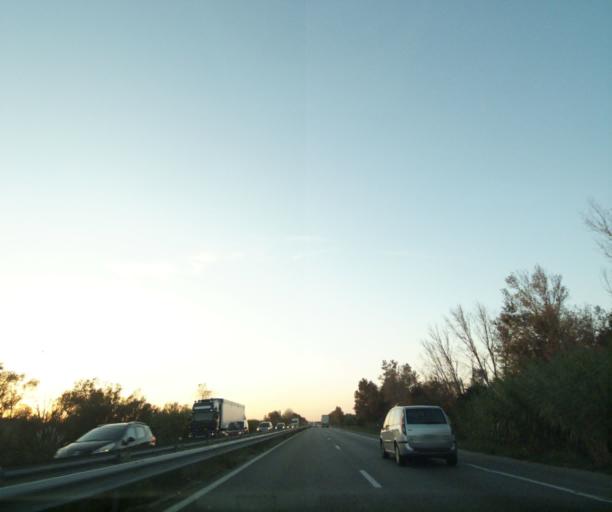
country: FR
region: Provence-Alpes-Cote d'Azur
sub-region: Departement des Bouches-du-Rhone
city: Saint-Martin-de-Crau
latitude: 43.6309
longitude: 4.7952
